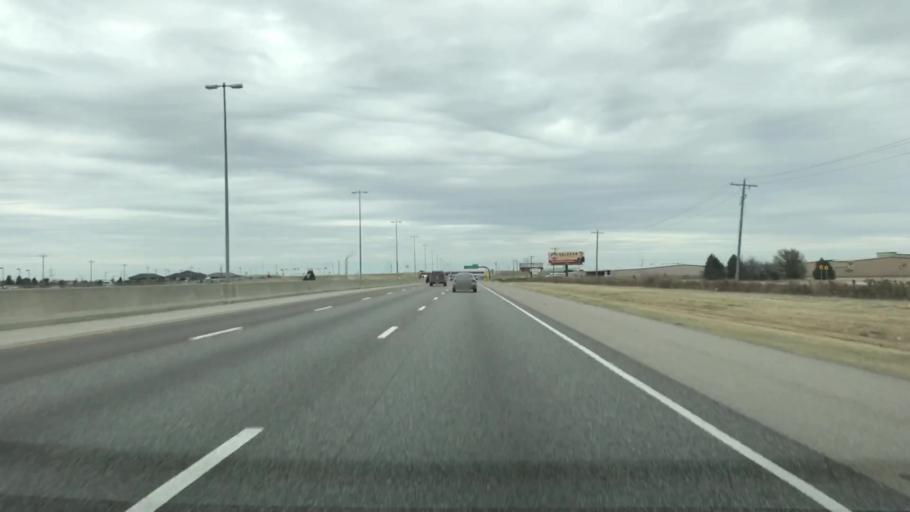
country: US
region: Oklahoma
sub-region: Cleveland County
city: Norman
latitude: 35.2552
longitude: -97.4854
